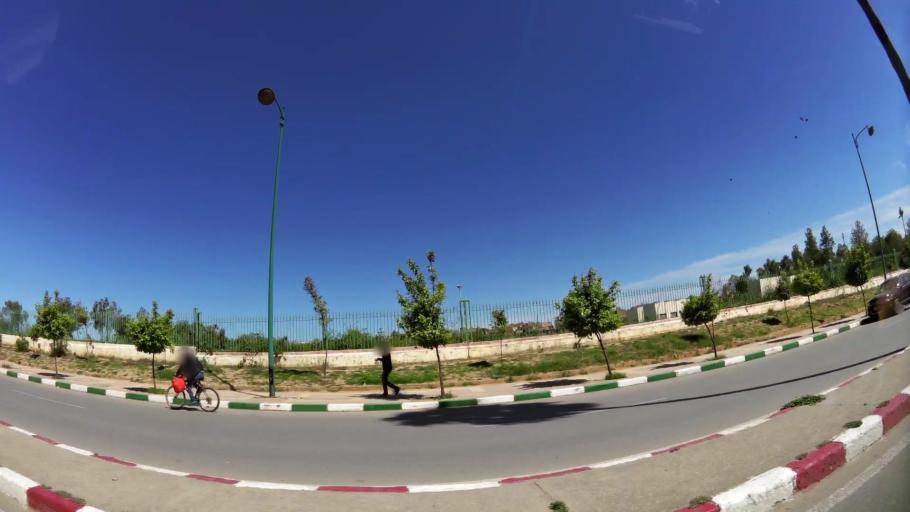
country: MA
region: Meknes-Tafilalet
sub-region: Meknes
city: Meknes
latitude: 33.8848
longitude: -5.5698
